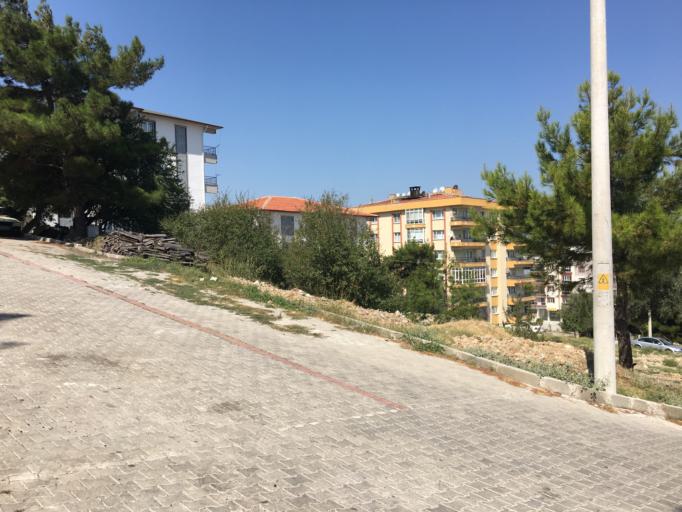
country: TR
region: Manisa
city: Soma
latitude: 39.1860
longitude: 27.5647
